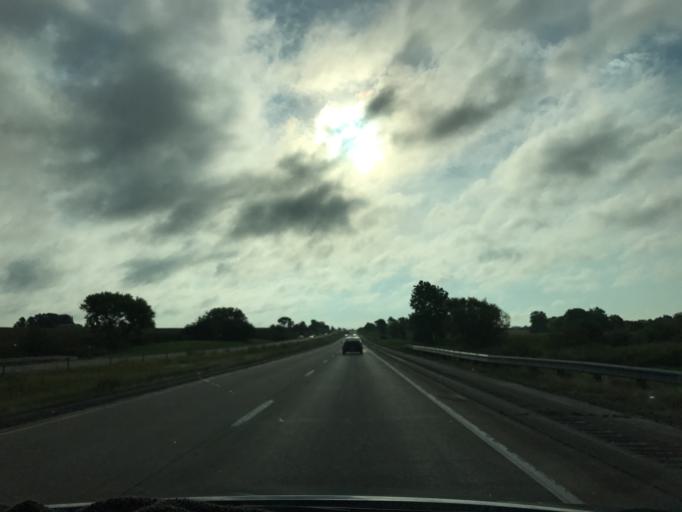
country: US
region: Iowa
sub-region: Cedar County
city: West Branch
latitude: 41.6673
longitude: -91.4114
